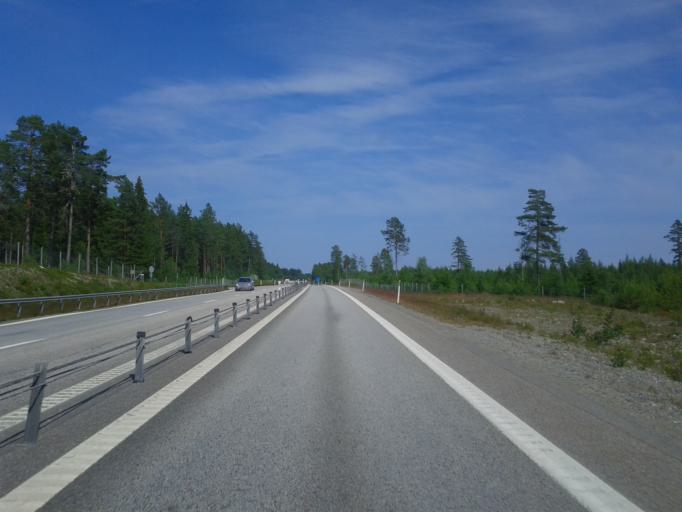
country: SE
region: Vaesterbotten
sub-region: Umea Kommun
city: Hoernefors
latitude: 63.6324
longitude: 19.8877
